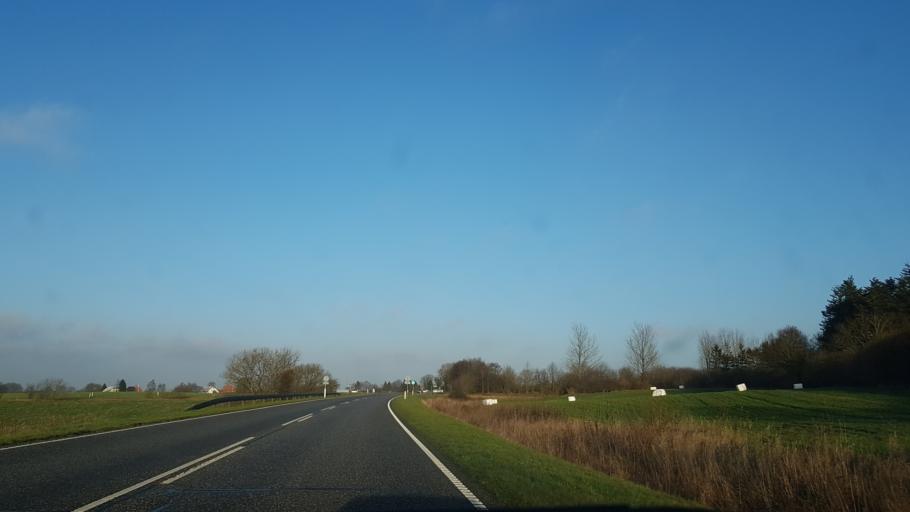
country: DK
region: South Denmark
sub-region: Haderslev Kommune
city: Haderslev
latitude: 55.2122
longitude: 9.4608
